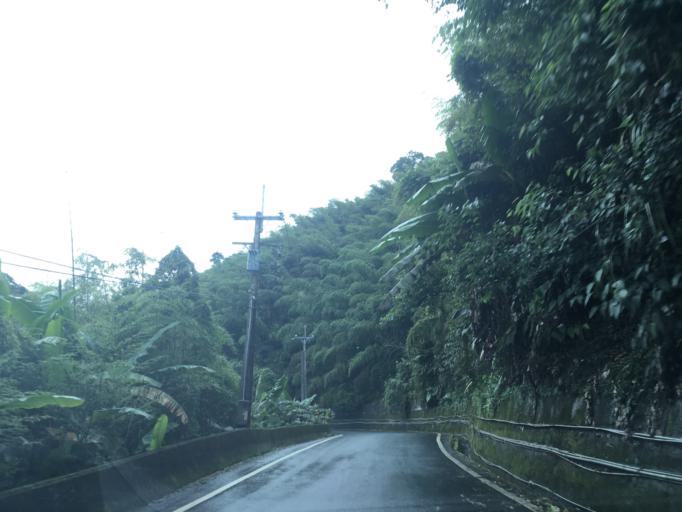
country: TW
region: Taiwan
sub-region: Chiayi
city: Jiayi Shi
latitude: 23.4450
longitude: 120.6690
